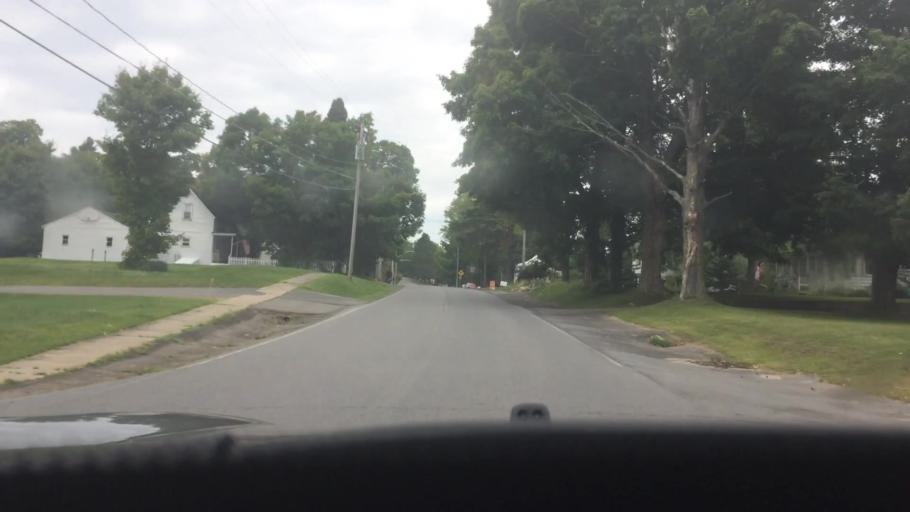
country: US
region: New York
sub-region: St. Lawrence County
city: Hannawa Falls
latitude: 44.5541
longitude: -74.9299
